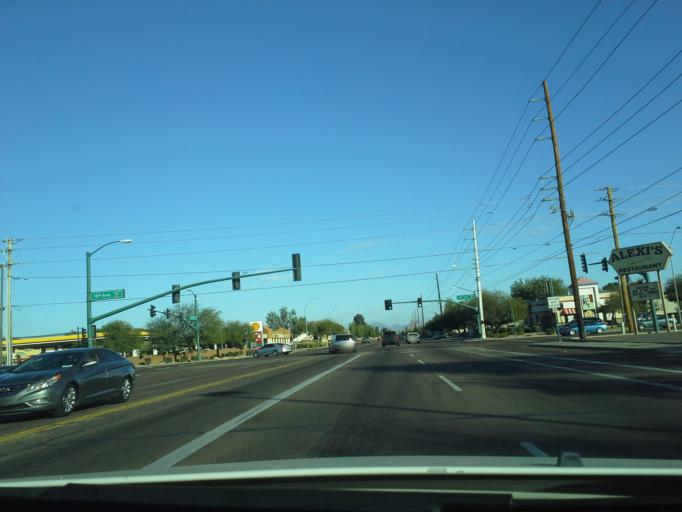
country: US
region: Arizona
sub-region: Maricopa County
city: Glendale
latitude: 33.6547
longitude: -112.1005
